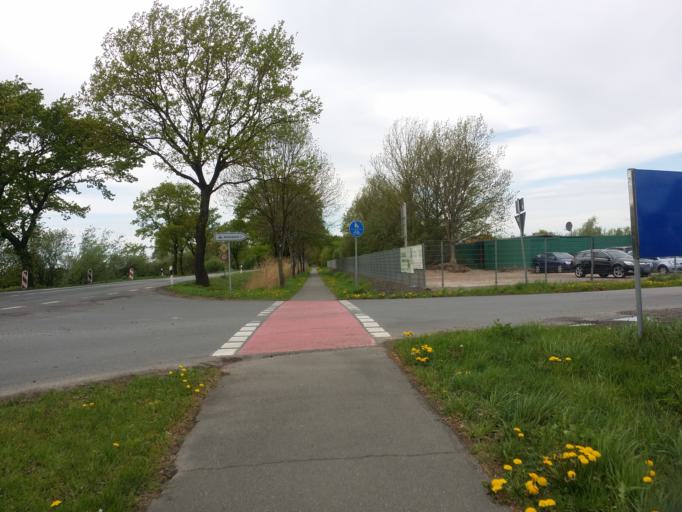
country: DE
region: Lower Saxony
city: Lemwerder
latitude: 53.1342
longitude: 8.6136
